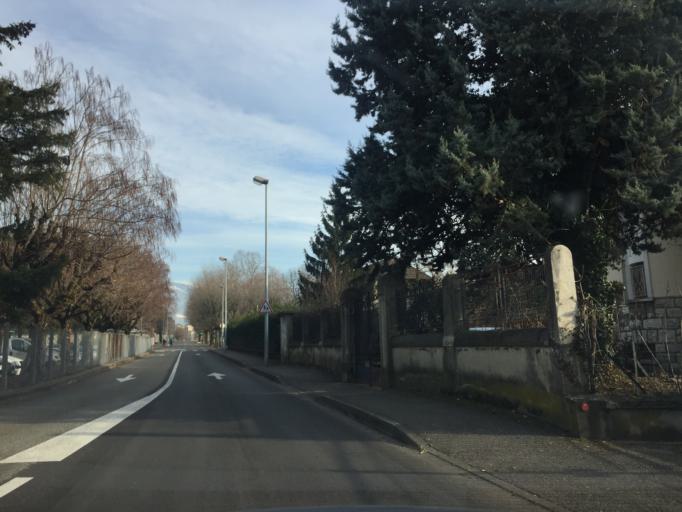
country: FR
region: Rhone-Alpes
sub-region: Departement de la Savoie
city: Cognin
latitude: 45.5765
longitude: 5.9035
